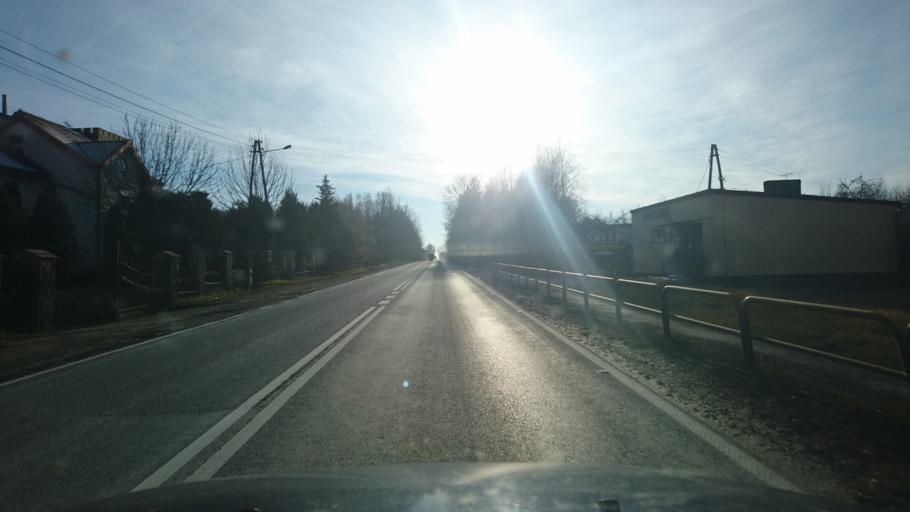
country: PL
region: Opole Voivodeship
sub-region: Powiat oleski
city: Dalachow
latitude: 51.0744
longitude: 18.6024
